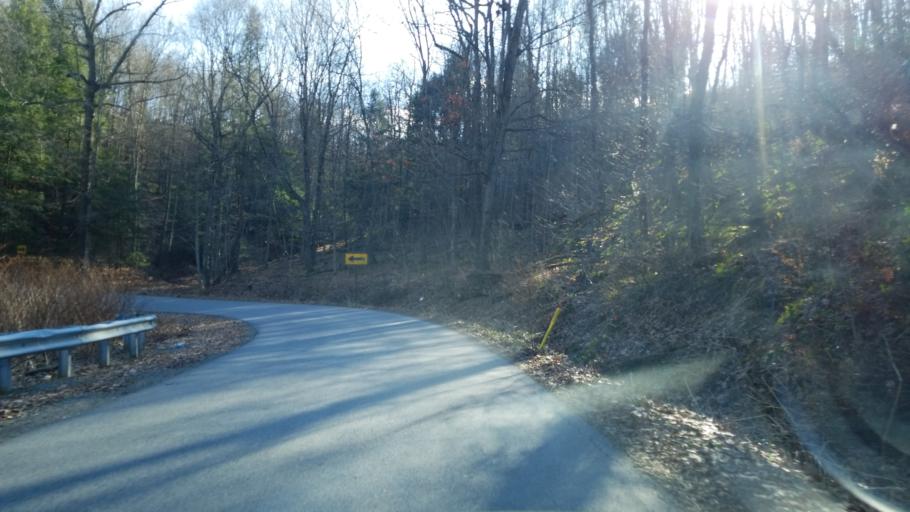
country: US
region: Pennsylvania
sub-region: Clearfield County
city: Hyde
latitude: 40.9849
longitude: -78.4765
